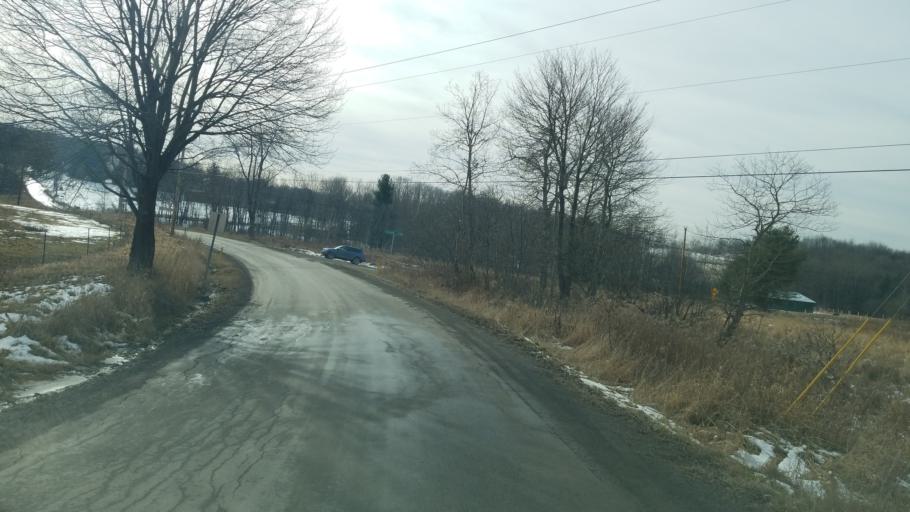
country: US
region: Pennsylvania
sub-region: Indiana County
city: Johnsonburg
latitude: 40.8405
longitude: -78.8723
